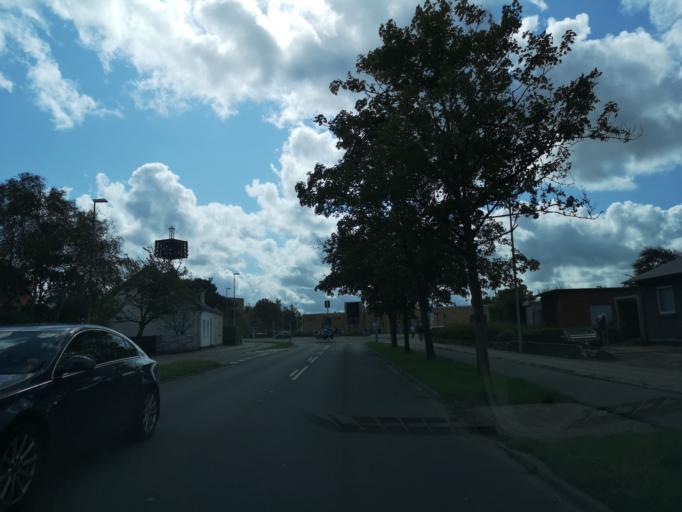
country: DK
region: Central Jutland
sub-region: Holstebro Kommune
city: Holstebro
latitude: 56.3661
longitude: 8.6085
